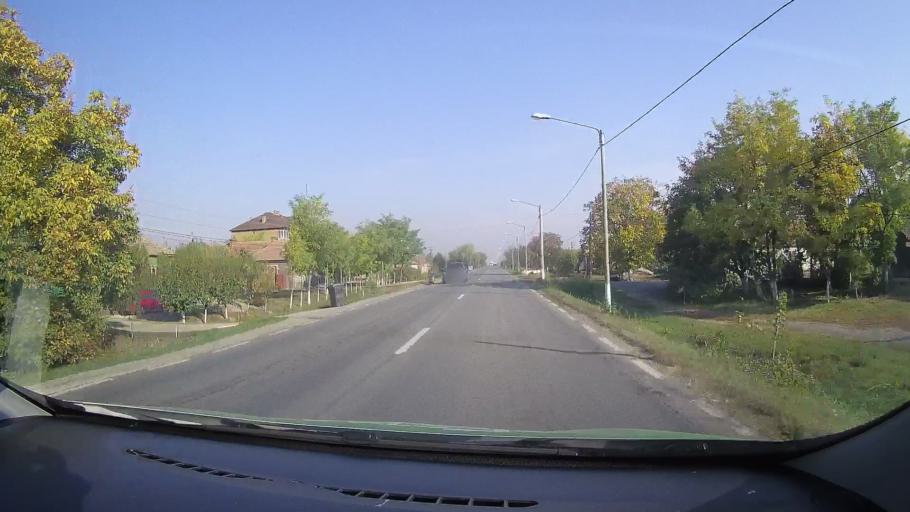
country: RO
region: Arad
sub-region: Comuna Pilu
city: Pilu
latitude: 46.5781
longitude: 21.3430
